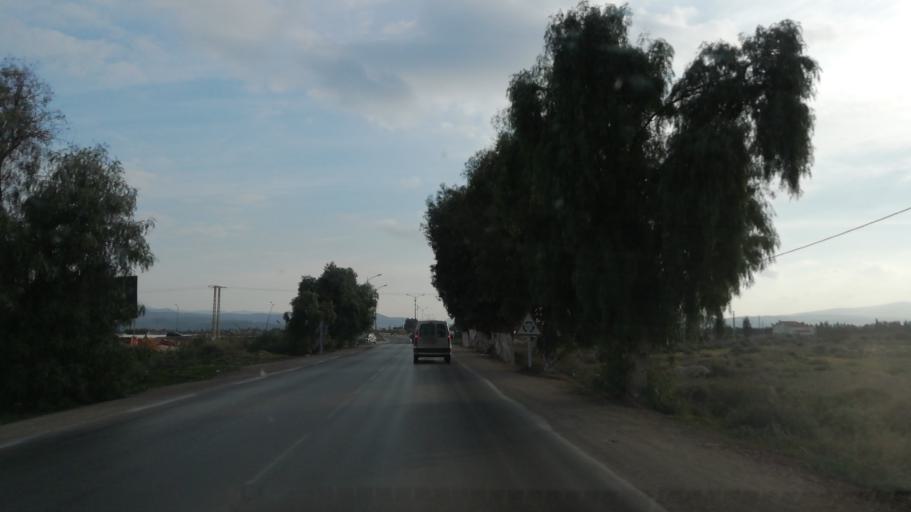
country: DZ
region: Mascara
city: Mascara
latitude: 35.6303
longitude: 0.0613
